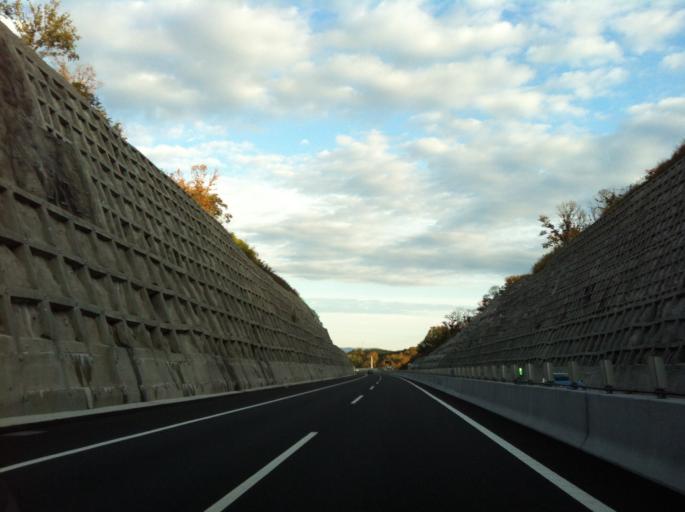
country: JP
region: Aichi
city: Okazaki
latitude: 35.0186
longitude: 137.2263
